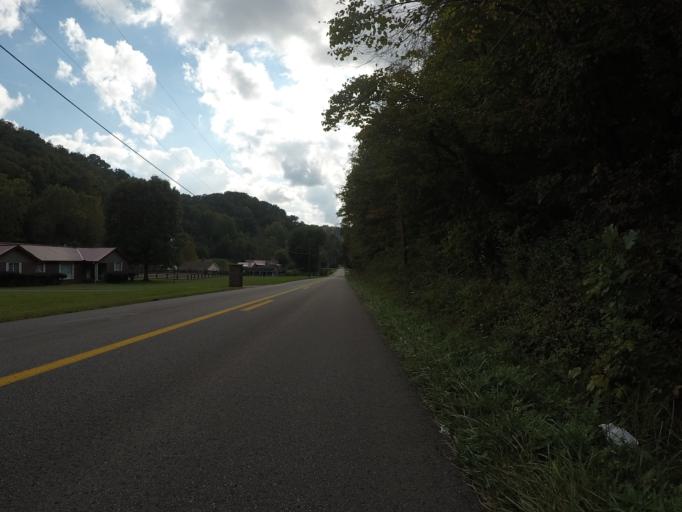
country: US
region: West Virginia
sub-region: Wayne County
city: Lavalette
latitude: 38.3511
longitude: -82.4462
